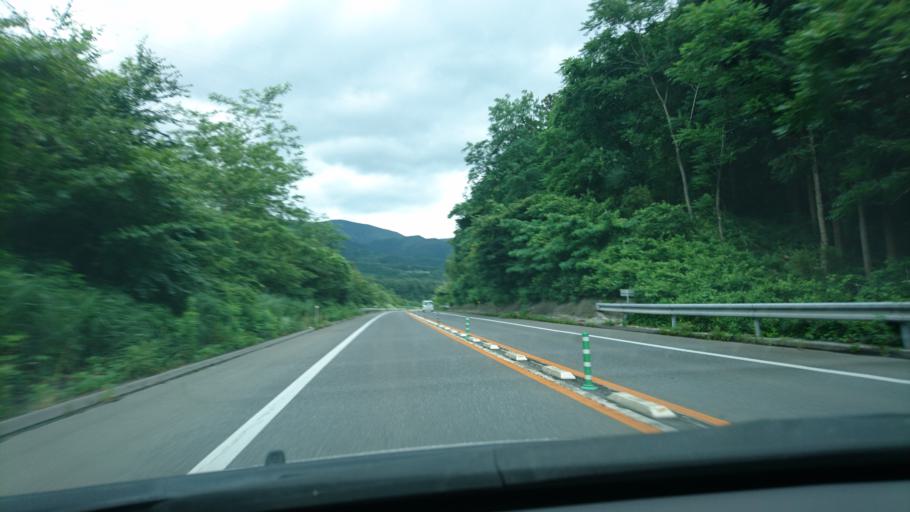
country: JP
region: Iwate
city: Ofunato
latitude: 39.1192
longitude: 141.7163
